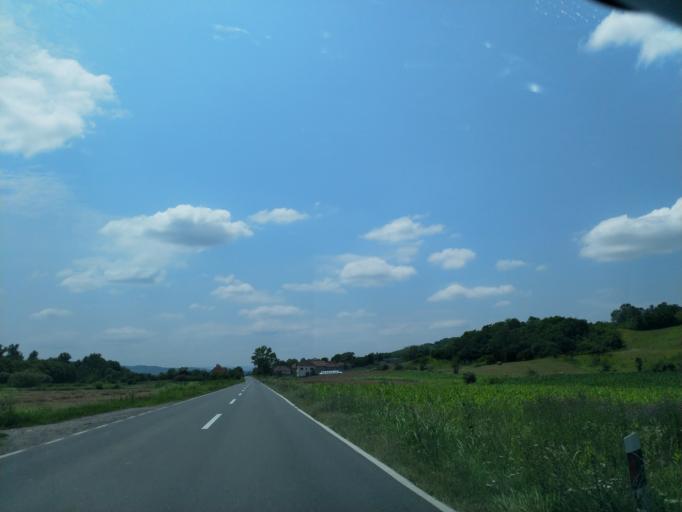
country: RS
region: Central Serbia
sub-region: Rasinski Okrug
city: Krusevac
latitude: 43.4790
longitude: 21.2680
